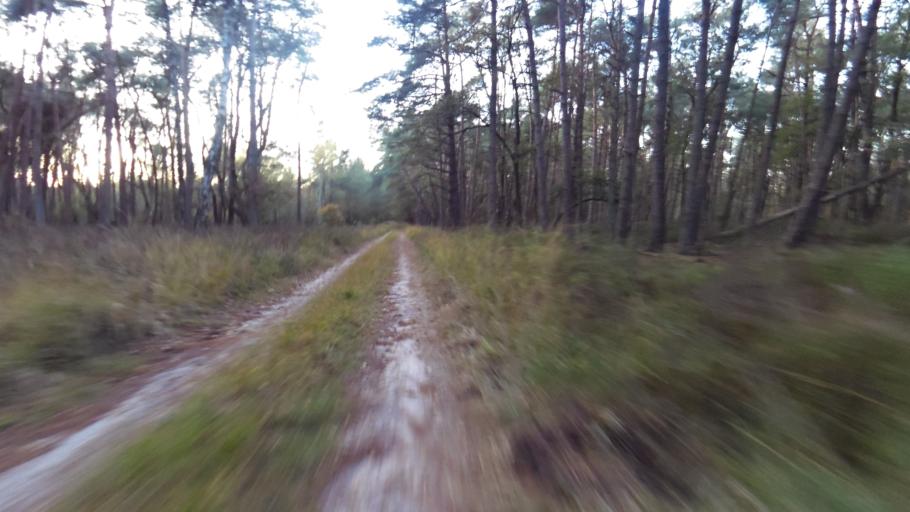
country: NL
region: Gelderland
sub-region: Gemeente Apeldoorn
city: Uddel
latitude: 52.2989
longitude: 5.8357
